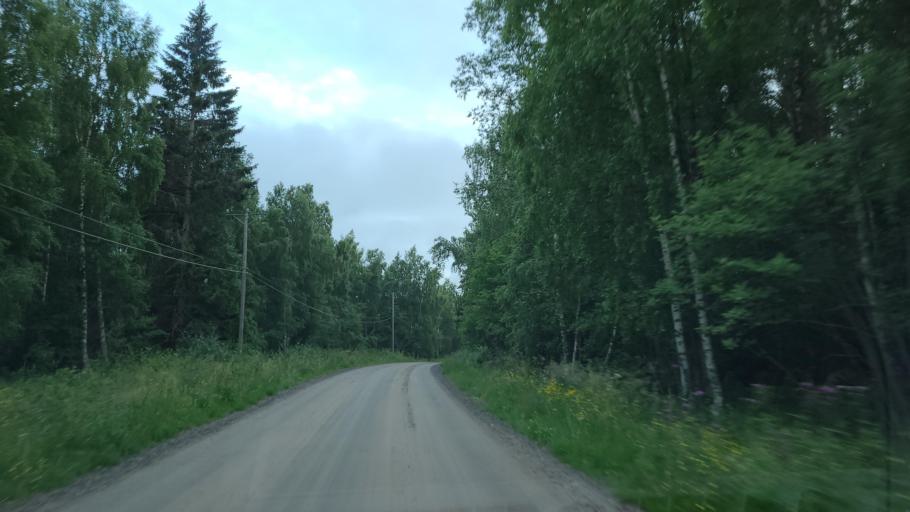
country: FI
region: Ostrobothnia
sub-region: Vaasa
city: Replot
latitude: 63.3010
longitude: 21.1481
